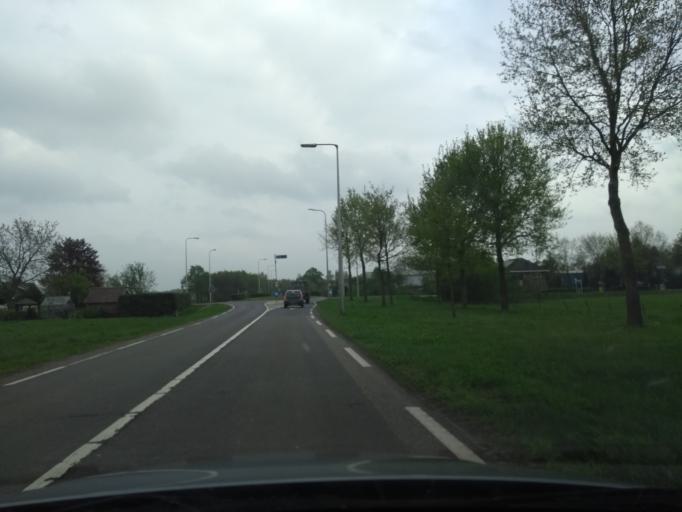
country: NL
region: Overijssel
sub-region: Gemeente Oldenzaal
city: Oldenzaal
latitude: 52.3579
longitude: 6.9245
